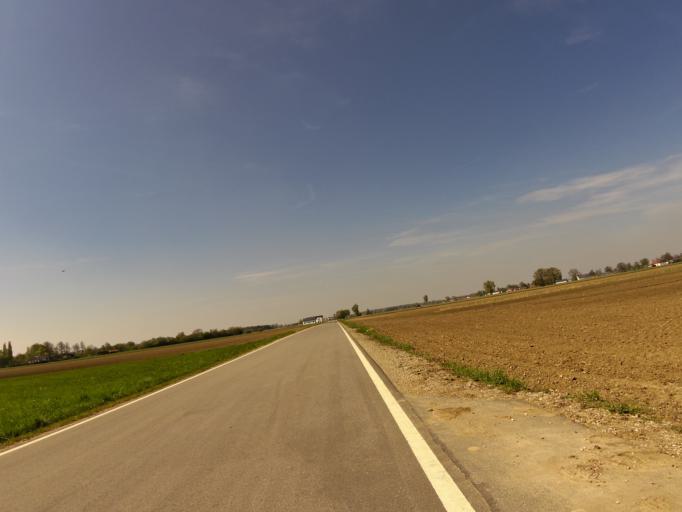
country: DE
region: Bavaria
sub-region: Upper Bavaria
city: Fraunberg
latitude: 48.3725
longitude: 11.9729
